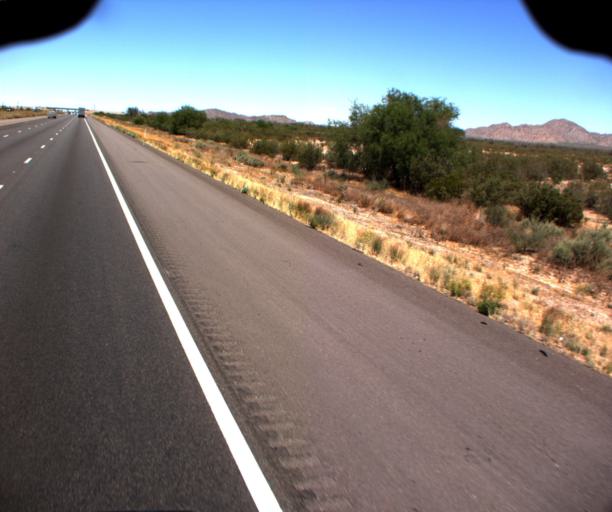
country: US
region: Arizona
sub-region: Pinal County
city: Casa Grande
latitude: 32.9590
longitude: -111.7173
